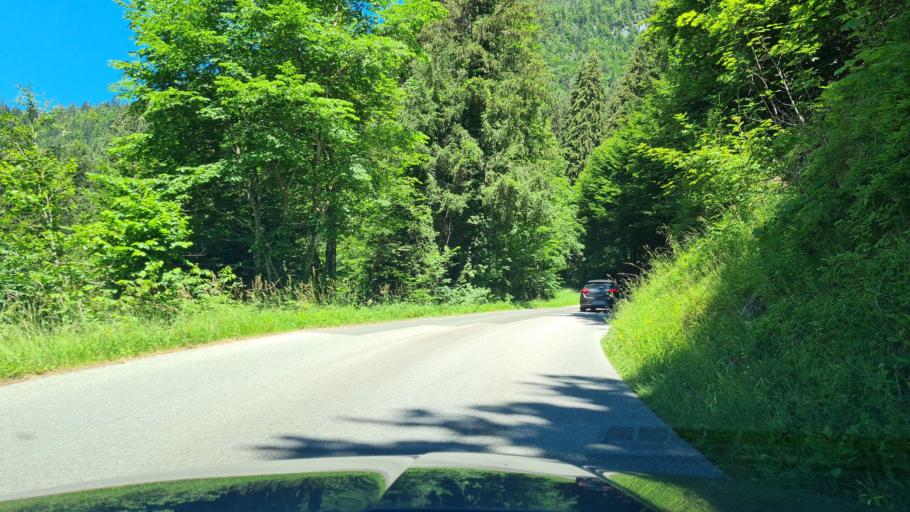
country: AT
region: Salzburg
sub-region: Politischer Bezirk Zell am See
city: Unken
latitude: 47.6490
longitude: 12.6932
